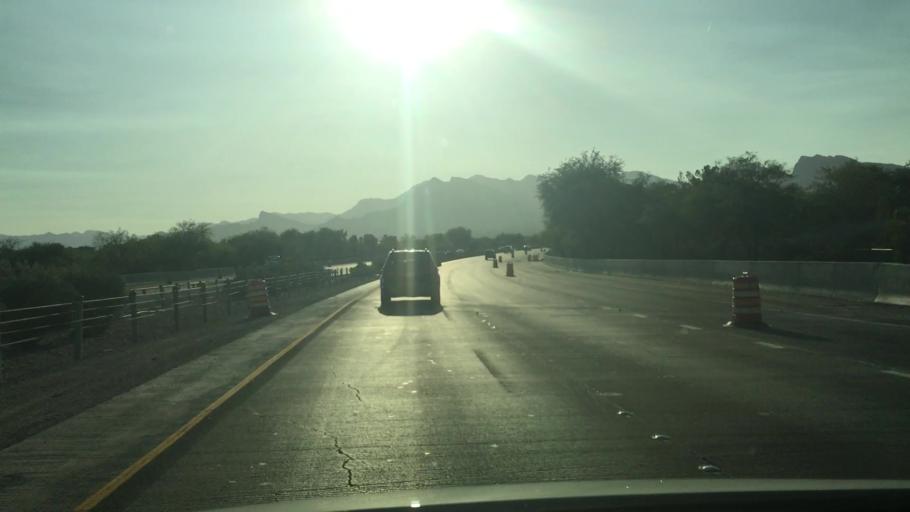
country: US
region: Nevada
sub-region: Clark County
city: Summerlin South
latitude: 36.1784
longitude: -115.2924
